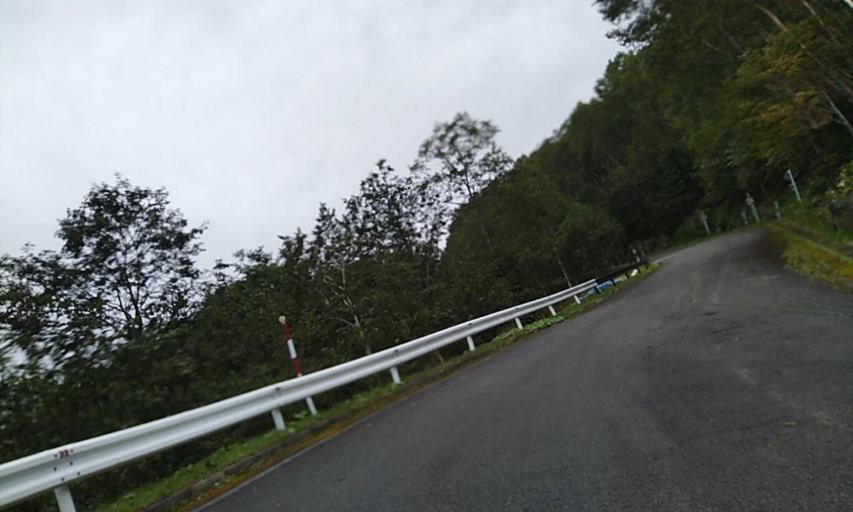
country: JP
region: Hokkaido
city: Bihoro
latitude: 43.5786
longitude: 144.2364
